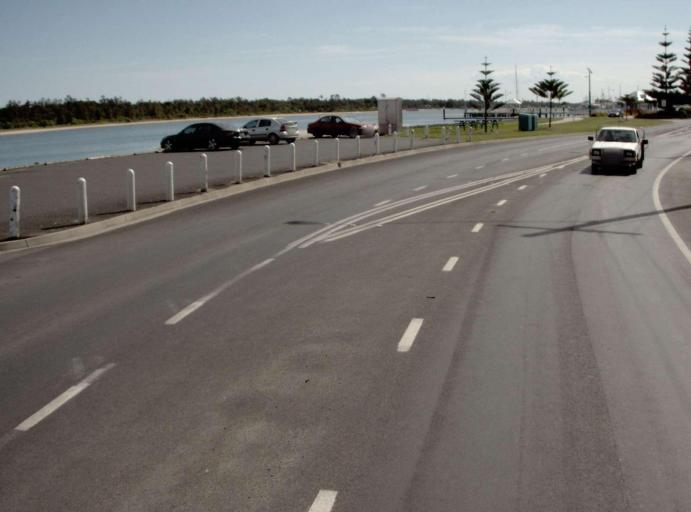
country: AU
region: Victoria
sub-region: East Gippsland
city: Lakes Entrance
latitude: -37.8810
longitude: 147.9873
